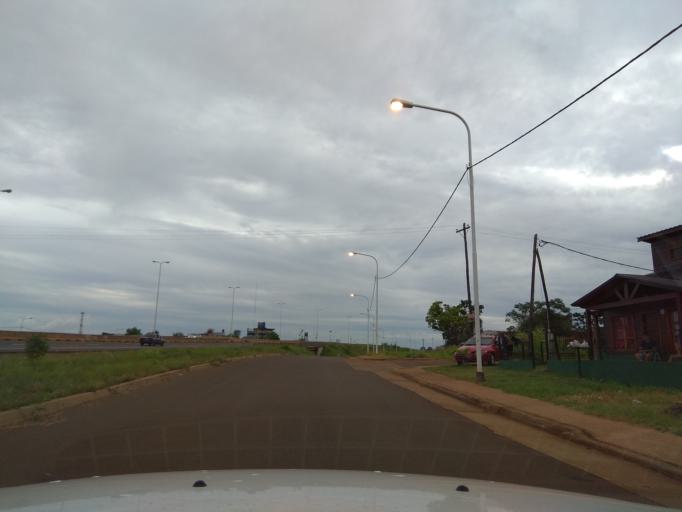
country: AR
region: Misiones
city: Garupa
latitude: -27.4508
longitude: -55.8562
